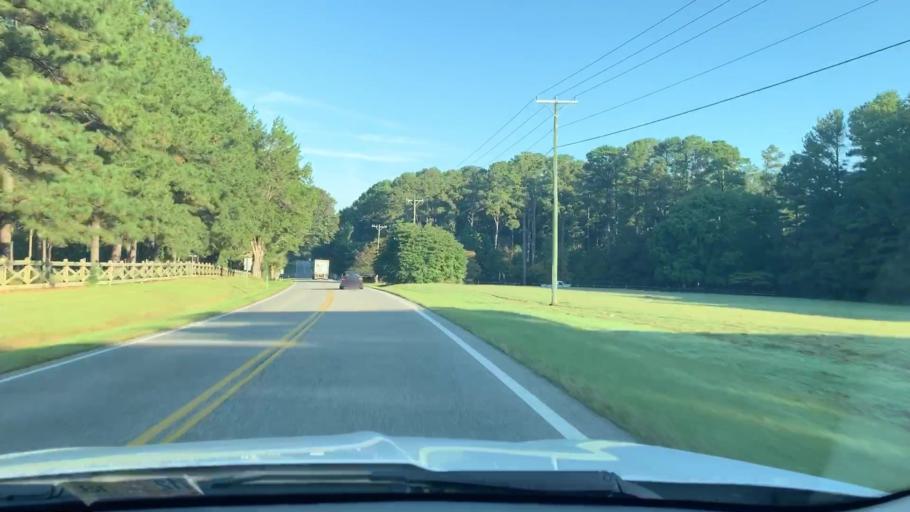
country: US
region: Virginia
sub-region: Middlesex County
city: Deltaville
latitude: 37.5170
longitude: -76.4203
